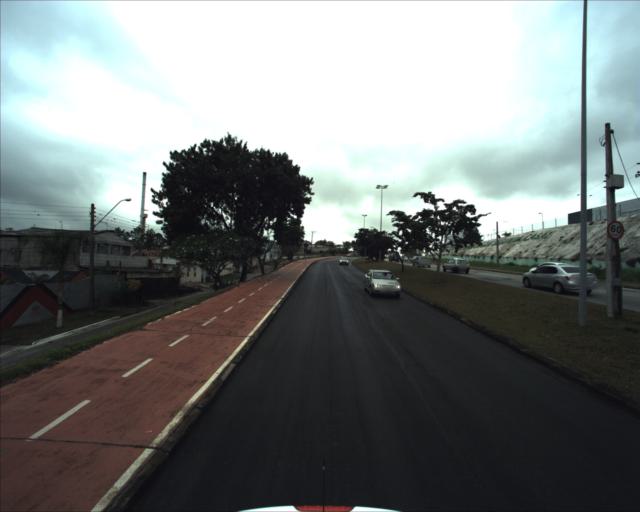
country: BR
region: Sao Paulo
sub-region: Votorantim
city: Votorantim
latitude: -23.5281
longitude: -47.4498
